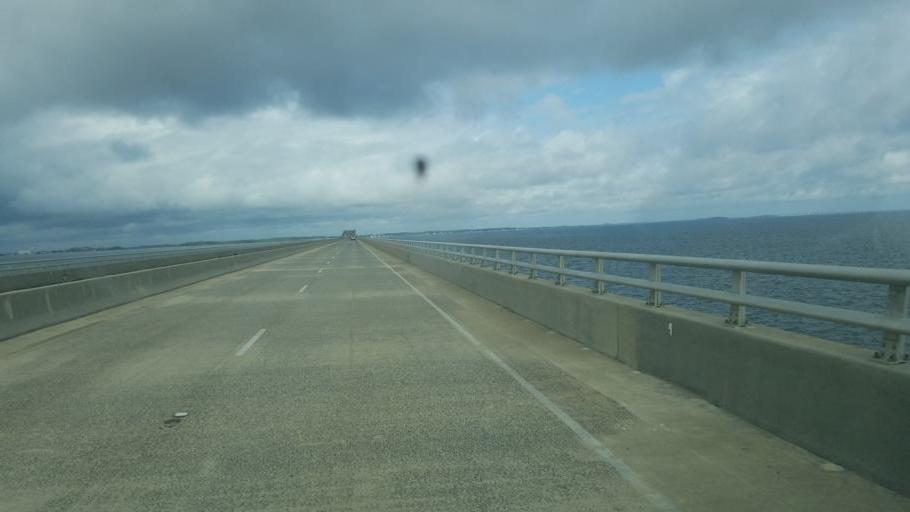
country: US
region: North Carolina
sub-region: Dare County
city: Manteo
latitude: 35.8837
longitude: -75.6998
